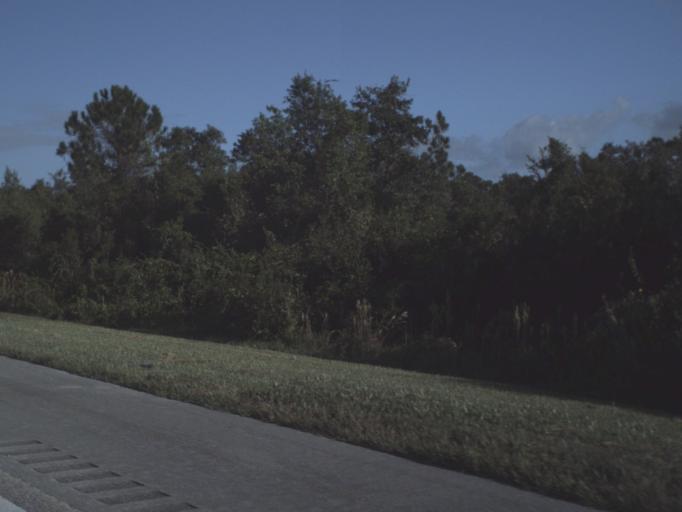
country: US
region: Florida
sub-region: Indian River County
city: Fellsmere
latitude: 27.7354
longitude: -80.9213
